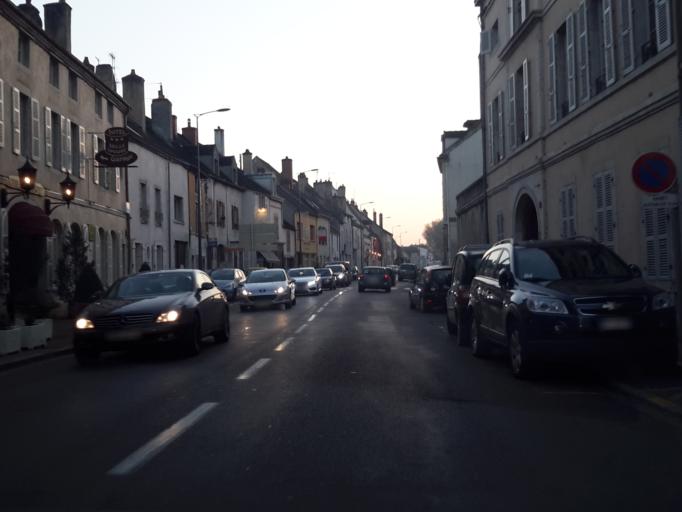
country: FR
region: Bourgogne
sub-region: Departement de la Cote-d'Or
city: Beaune
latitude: 47.0216
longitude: 4.8328
